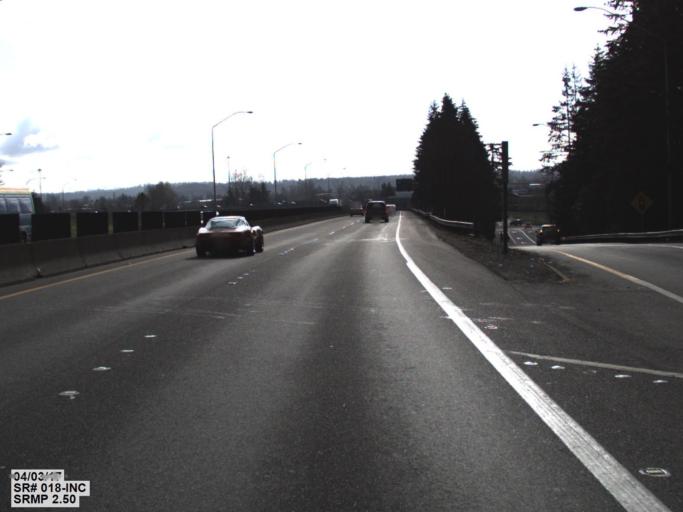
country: US
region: Washington
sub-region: King County
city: Algona
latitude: 47.3036
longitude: -122.2605
